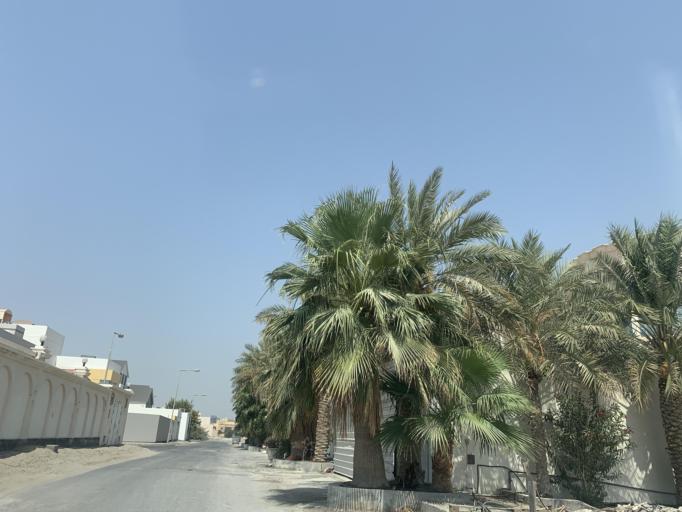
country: BH
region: Manama
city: Jidd Hafs
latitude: 26.1982
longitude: 50.5243
